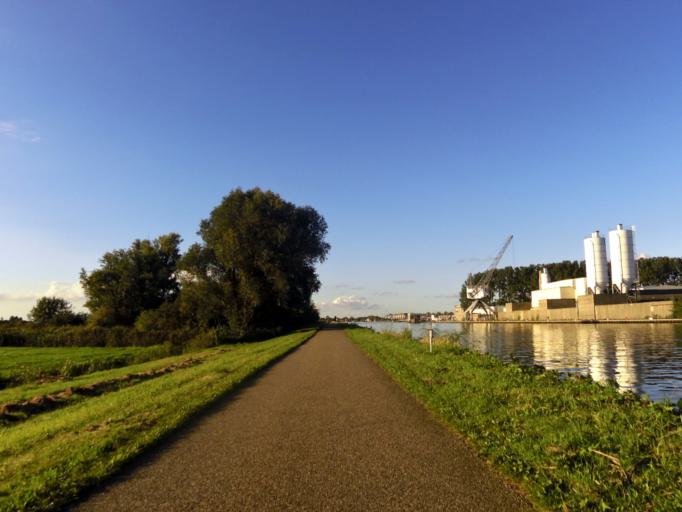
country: NL
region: South Holland
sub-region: Gemeente Alphen aan den Rijn
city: Alphen aan den Rijn
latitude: 52.1501
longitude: 4.6449
